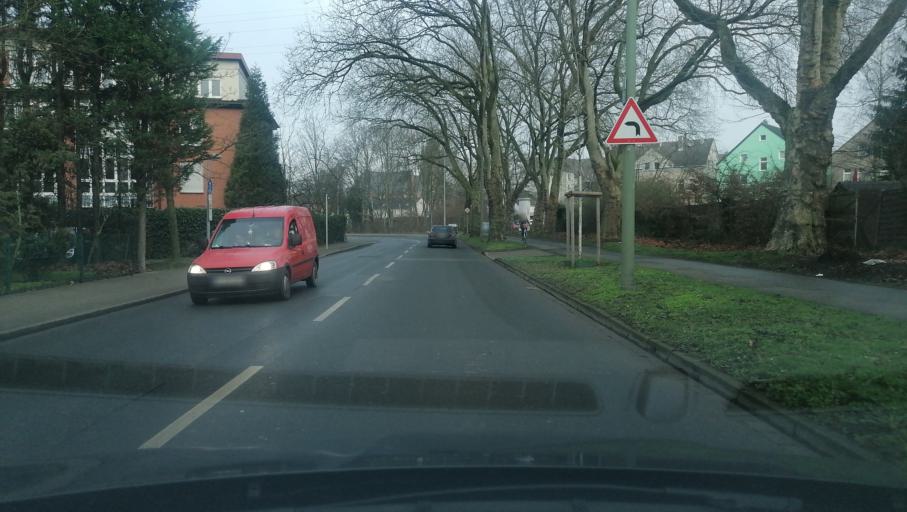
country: DE
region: North Rhine-Westphalia
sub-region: Regierungsbezirk Munster
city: Gelsenkirchen
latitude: 51.5234
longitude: 7.1056
